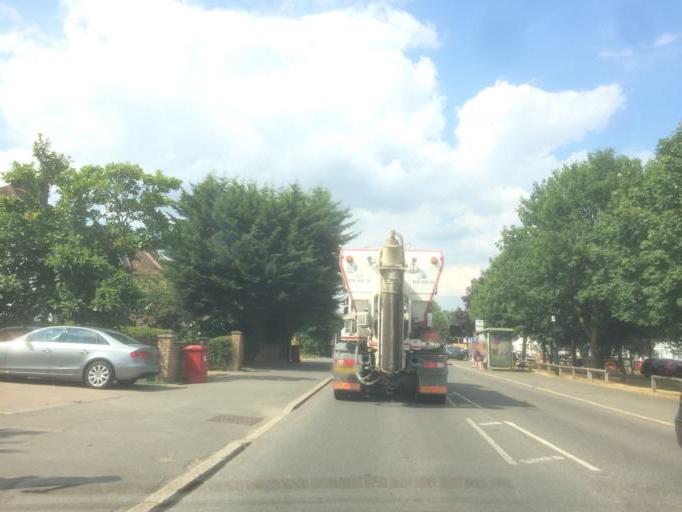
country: GB
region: England
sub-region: Buckinghamshire
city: Farnham Royal
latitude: 51.5313
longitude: -0.6176
